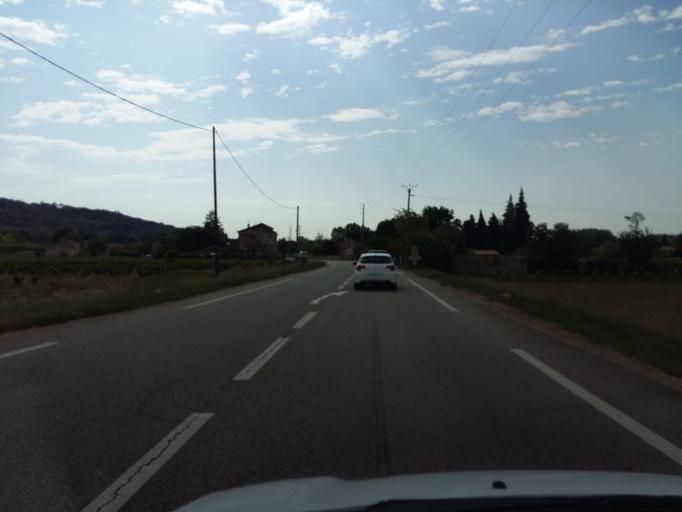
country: FR
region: Provence-Alpes-Cote d'Azur
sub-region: Departement du Vaucluse
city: Bollene
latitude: 44.2804
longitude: 4.7910
